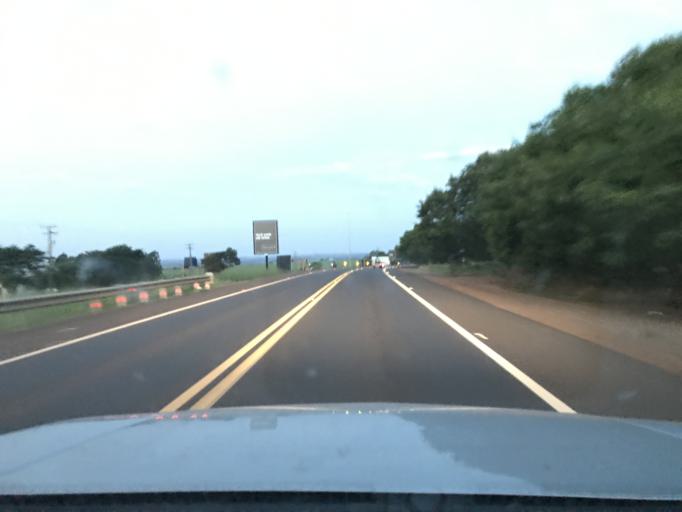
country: PY
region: Canindeyu
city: Salto del Guaira
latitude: -24.0120
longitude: -54.3028
